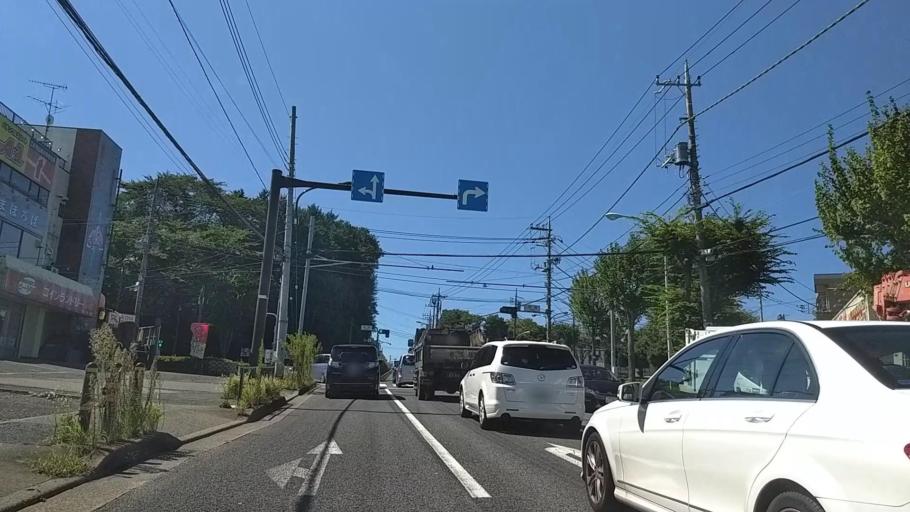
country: JP
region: Tokyo
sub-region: Machida-shi
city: Machida
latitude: 35.5803
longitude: 139.4167
